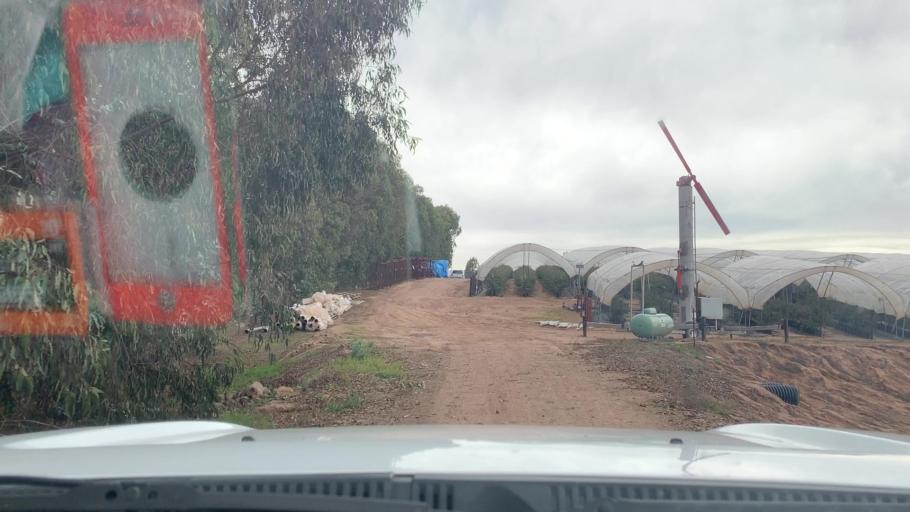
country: US
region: California
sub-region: San Luis Obispo County
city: Callender
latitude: 35.0608
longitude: -120.5668
